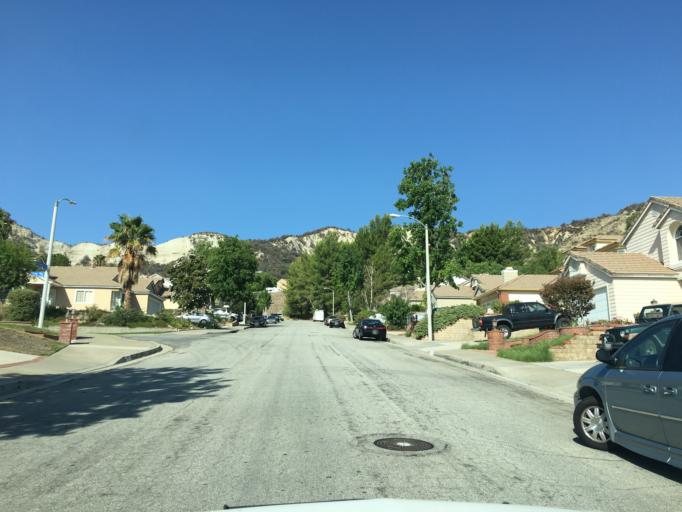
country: US
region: California
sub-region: Los Angeles County
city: Castaic
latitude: 34.4872
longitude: -118.6367
